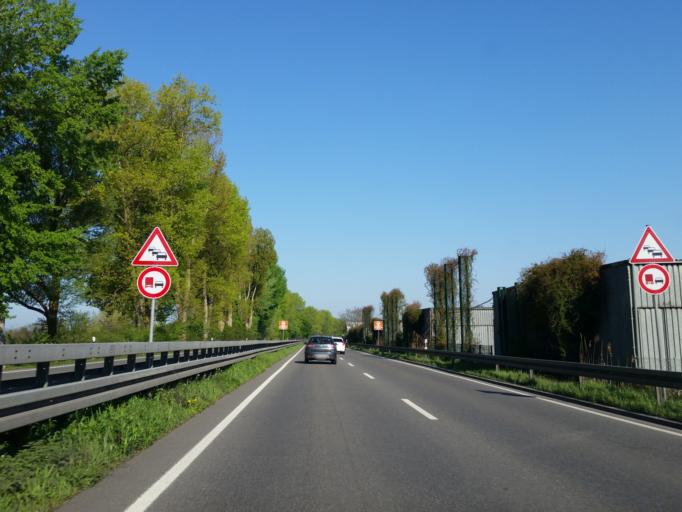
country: CH
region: Thurgau
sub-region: Kreuzlingen District
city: Gottlieben
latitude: 47.6811
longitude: 9.1370
